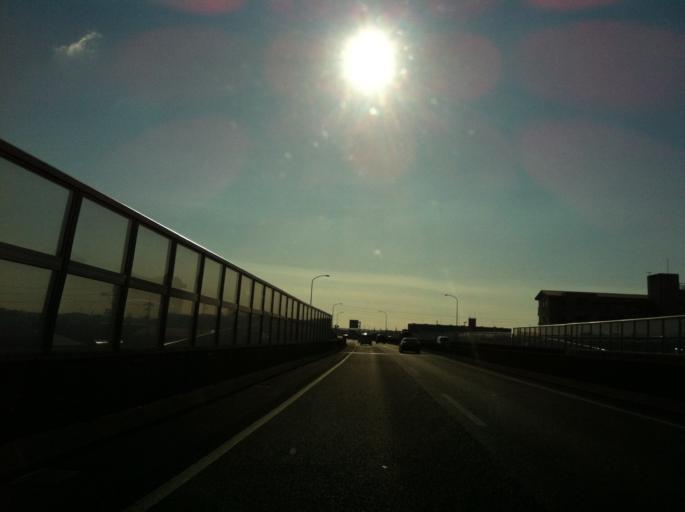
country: JP
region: Aichi
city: Toyohashi
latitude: 34.7389
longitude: 137.3436
